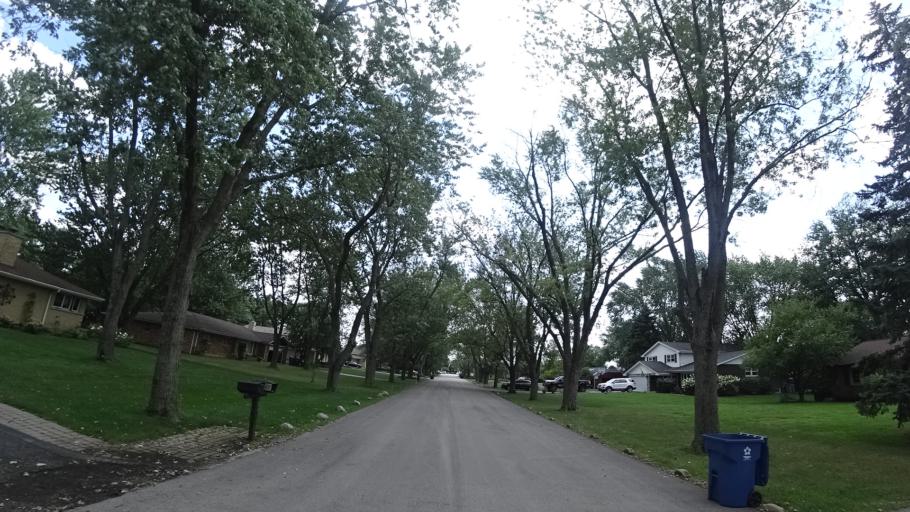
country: US
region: Illinois
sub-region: Cook County
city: Orland Park
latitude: 41.6185
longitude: -87.8159
